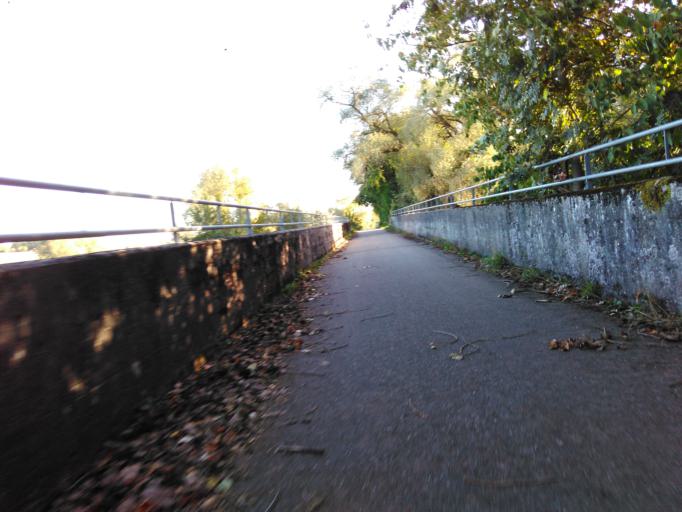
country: FR
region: Lorraine
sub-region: Departement de la Moselle
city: Bousse
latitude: 49.2879
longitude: 6.1816
